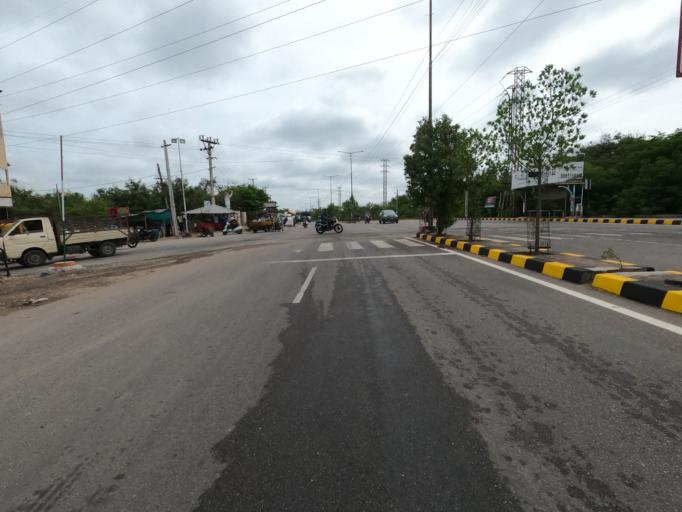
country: IN
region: Telangana
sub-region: Hyderabad
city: Hyderabad
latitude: 17.3366
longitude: 78.4116
